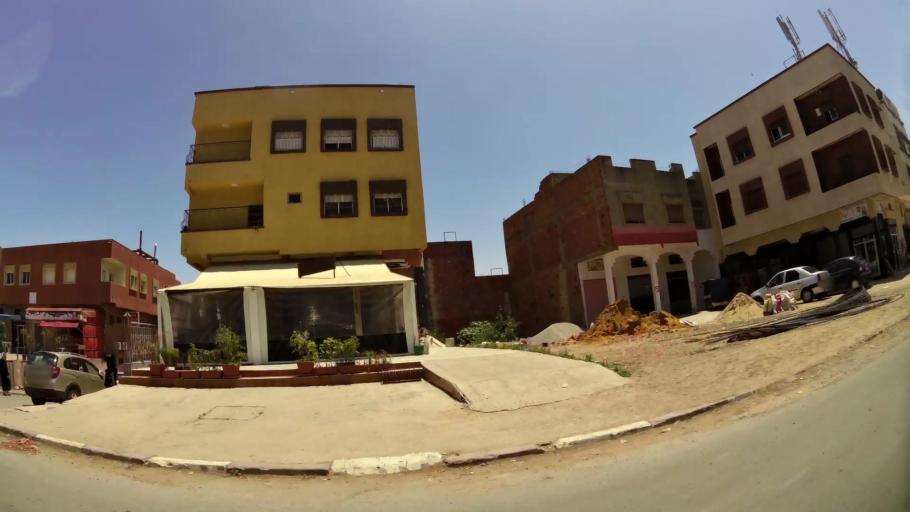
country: MA
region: Gharb-Chrarda-Beni Hssen
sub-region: Kenitra Province
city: Kenitra
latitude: 34.2621
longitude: -6.6441
